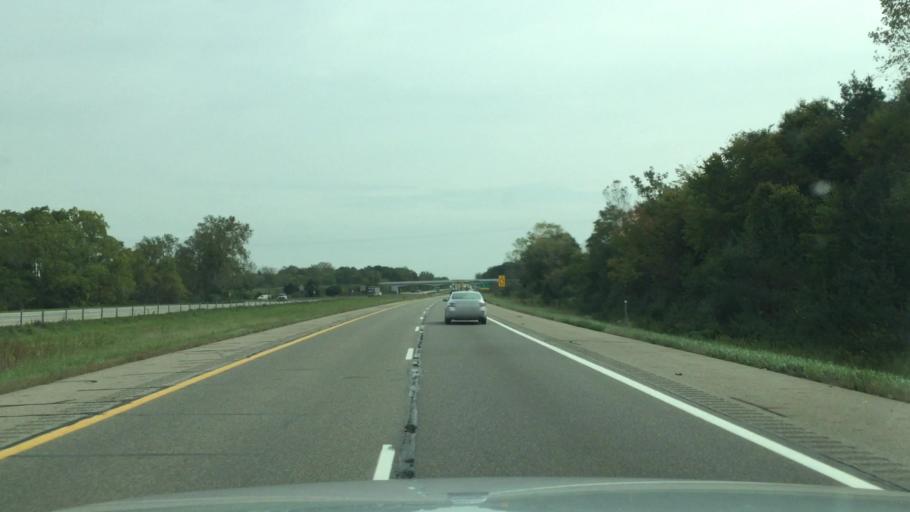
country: US
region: Michigan
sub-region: Shiawassee County
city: Durand
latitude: 42.9640
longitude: -83.9354
